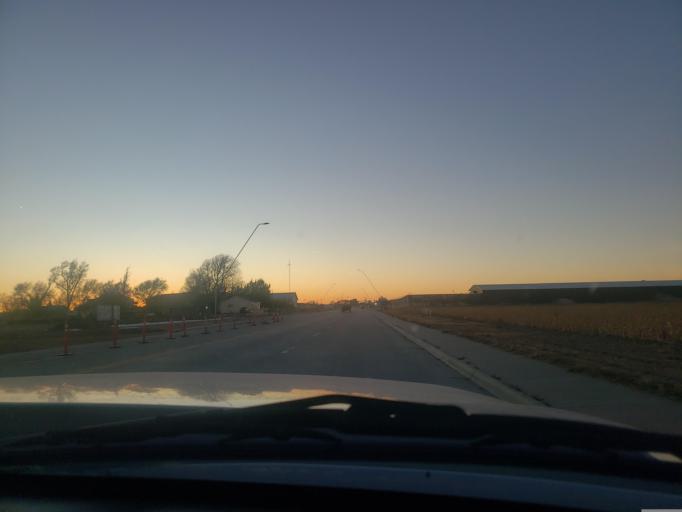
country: US
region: Kansas
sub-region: Finney County
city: Garden City
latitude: 37.9748
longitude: -100.8315
